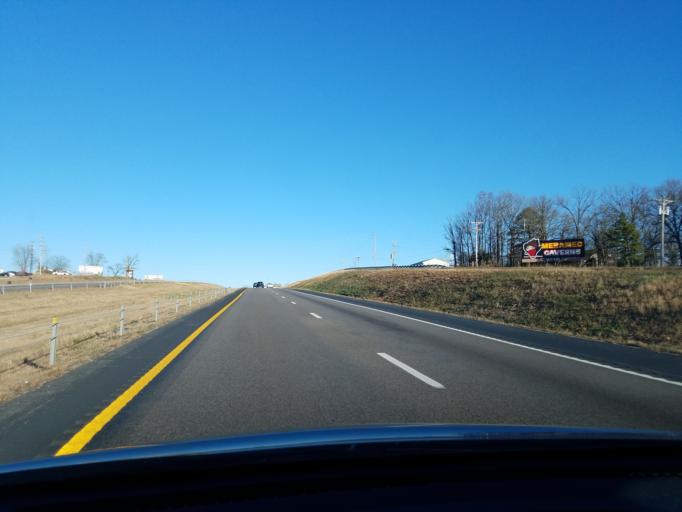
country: US
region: Missouri
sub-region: Phelps County
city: Saint James
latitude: 37.9924
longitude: -91.6416
